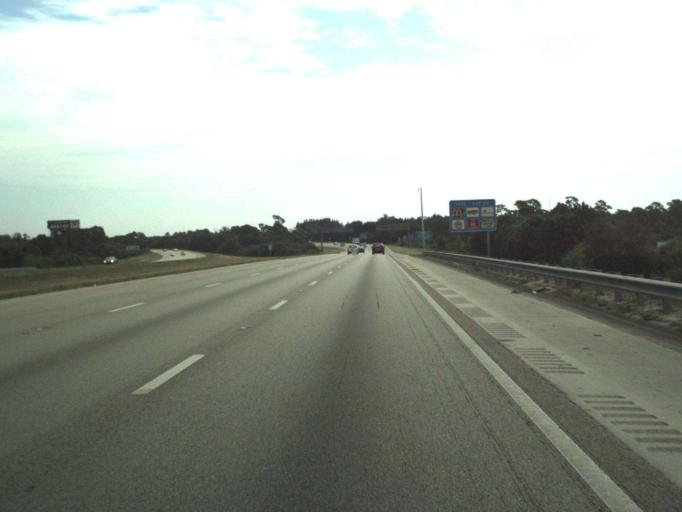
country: US
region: Florida
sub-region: Saint Lucie County
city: Fort Pierce South
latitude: 27.3965
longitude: -80.3931
